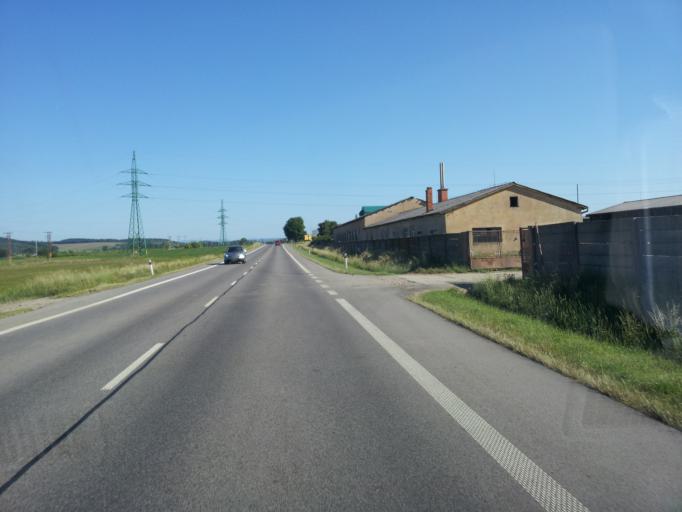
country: SK
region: Nitriansky
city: Sahy
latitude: 48.0950
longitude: 18.8953
